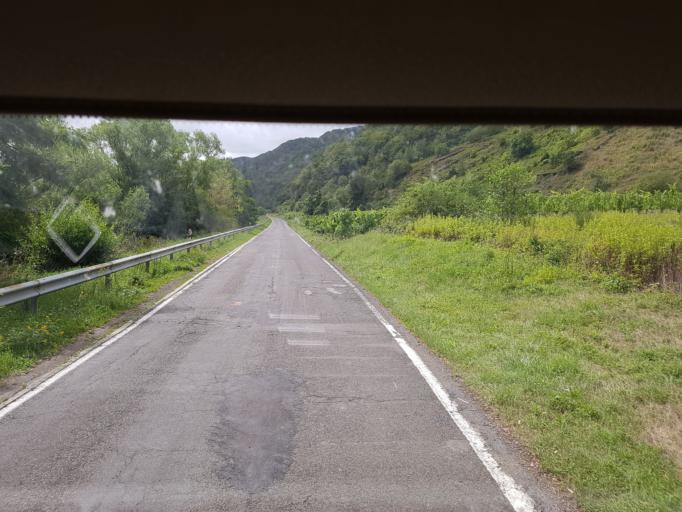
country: DE
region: Rheinland-Pfalz
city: Enkirch
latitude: 49.9986
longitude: 7.1138
